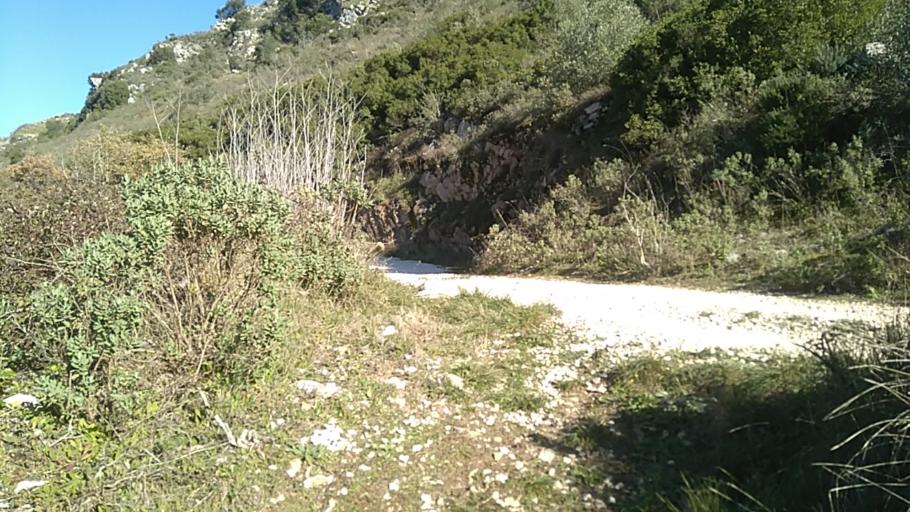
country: PT
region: Leiria
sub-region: Porto de Mos
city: Porto de Mos
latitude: 39.5580
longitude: -8.8359
